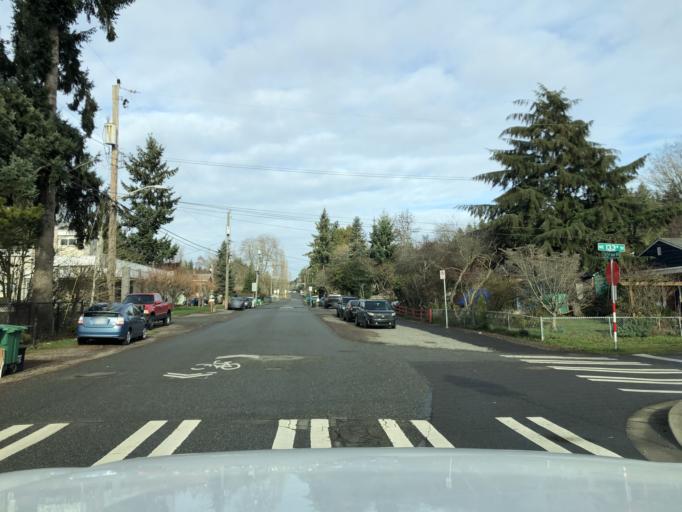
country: US
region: Washington
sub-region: King County
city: Lake Forest Park
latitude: 47.7247
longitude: -122.3073
